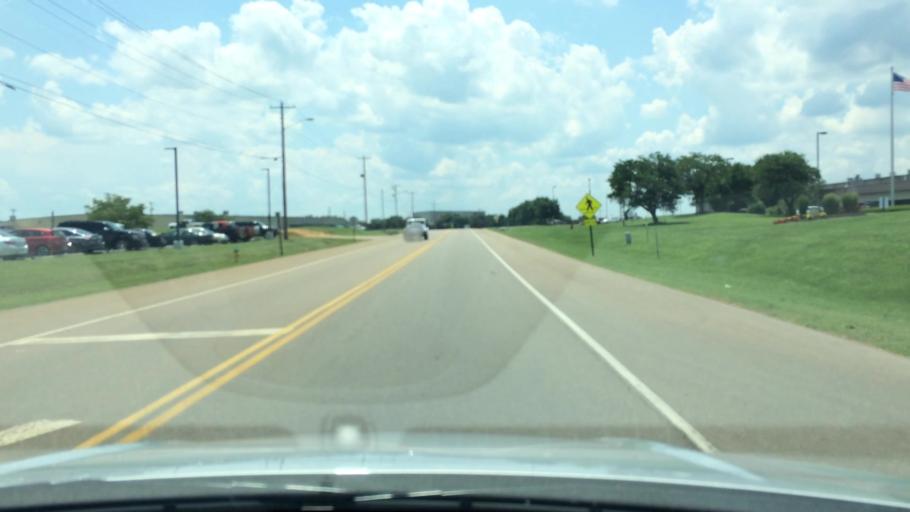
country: US
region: Tennessee
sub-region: Jefferson County
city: Jefferson City
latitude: 36.1655
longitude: -83.3943
